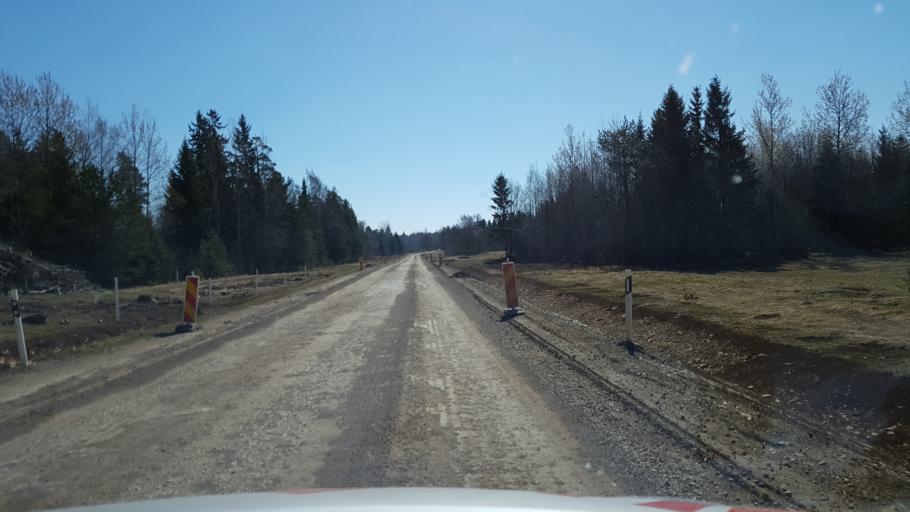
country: EE
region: Laeaene-Virumaa
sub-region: Vinni vald
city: Vinni
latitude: 59.0610
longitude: 26.6429
